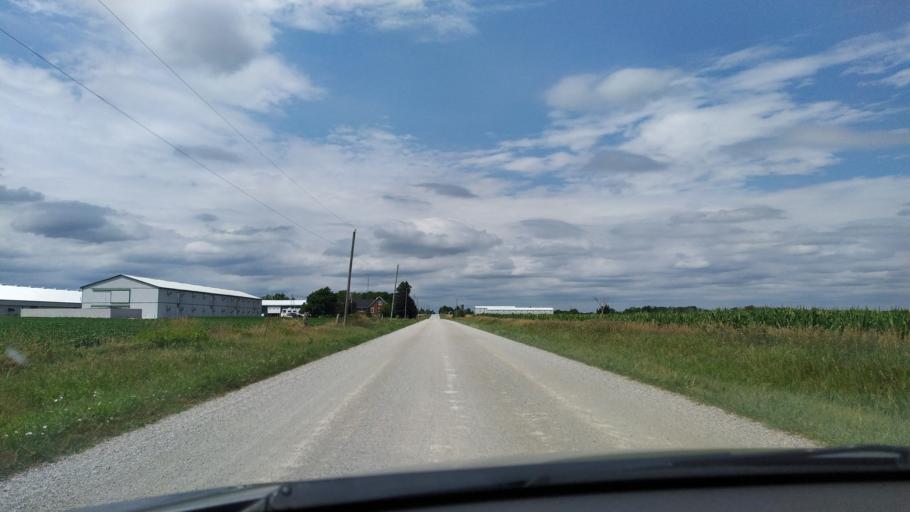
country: CA
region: Ontario
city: Stratford
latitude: 43.3577
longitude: -80.9126
